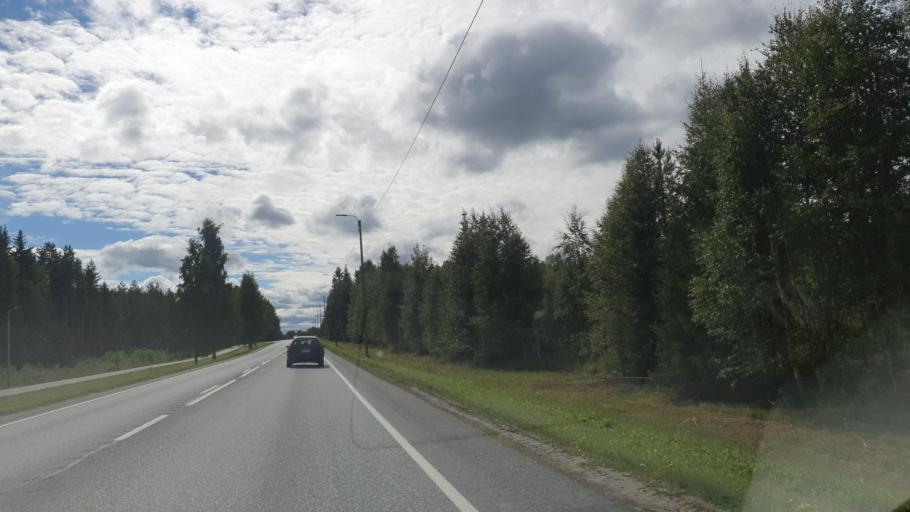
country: FI
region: Kainuu
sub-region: Kajaani
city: Kajaani
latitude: 64.2021
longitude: 27.6402
